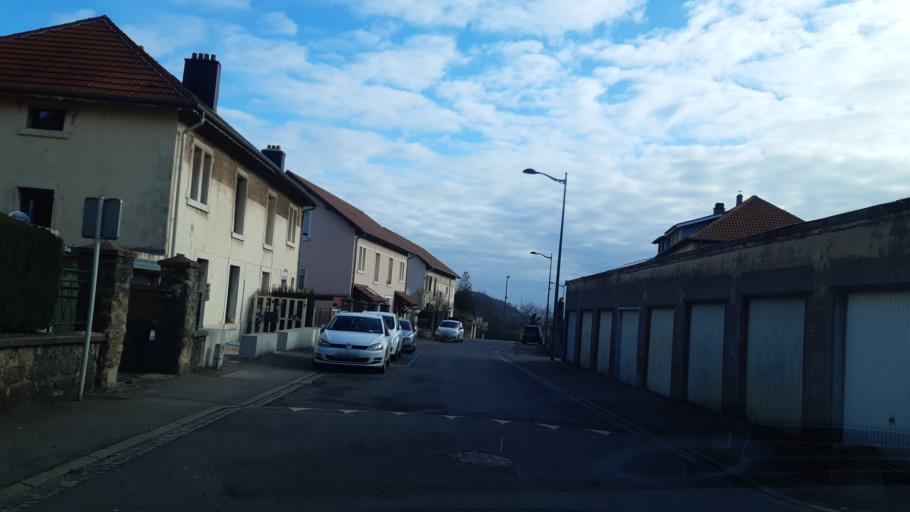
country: FR
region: Lorraine
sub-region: Departement de Meurthe-et-Moselle
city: Villerupt
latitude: 49.4721
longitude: 5.9347
